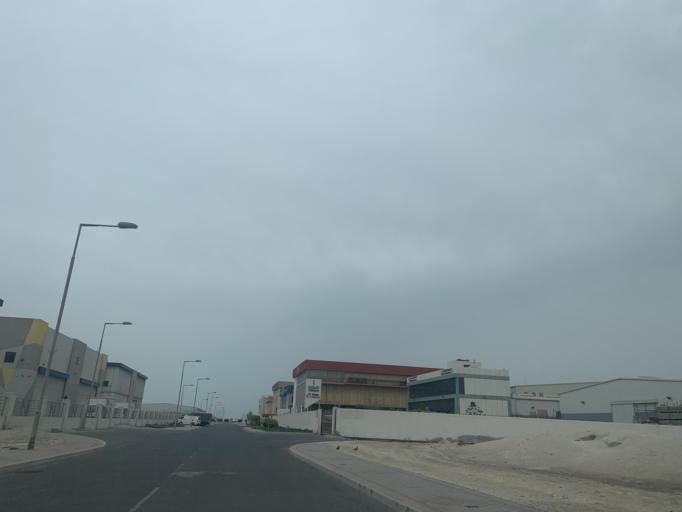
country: BH
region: Muharraq
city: Al Hadd
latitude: 26.2118
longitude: 50.6751
